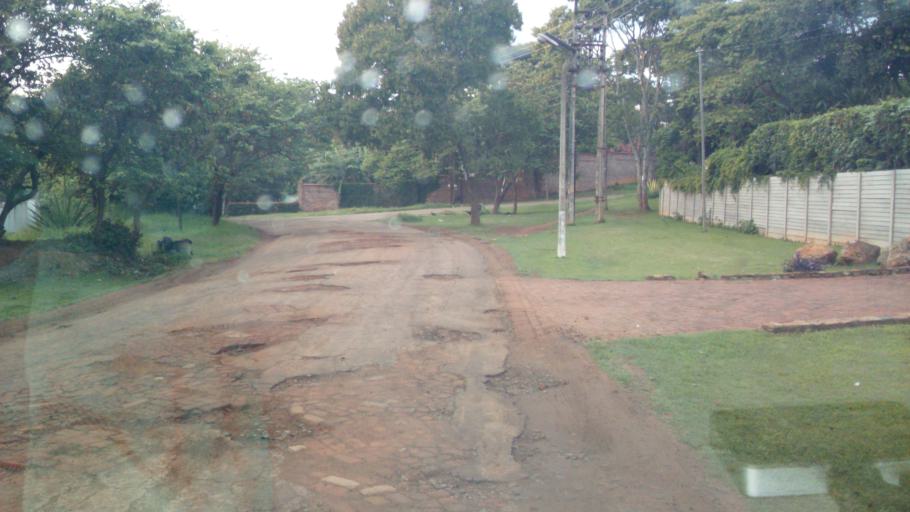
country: ZW
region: Harare
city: Harare
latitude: -17.7736
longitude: 31.1039
